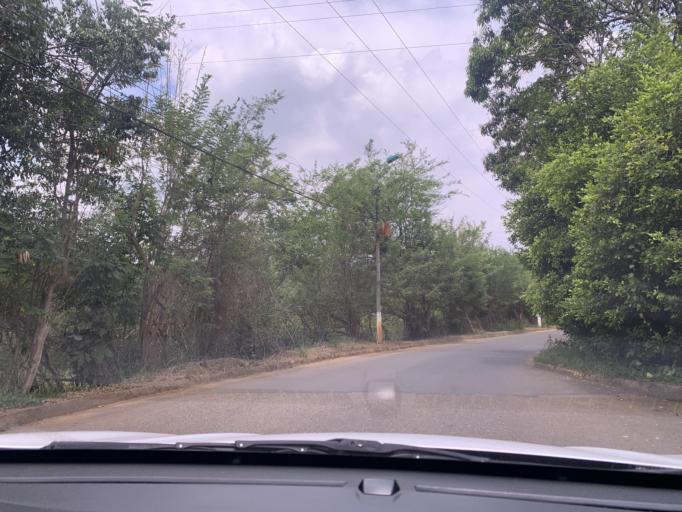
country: CO
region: Valle del Cauca
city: Jamundi
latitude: 3.3373
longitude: -76.5522
